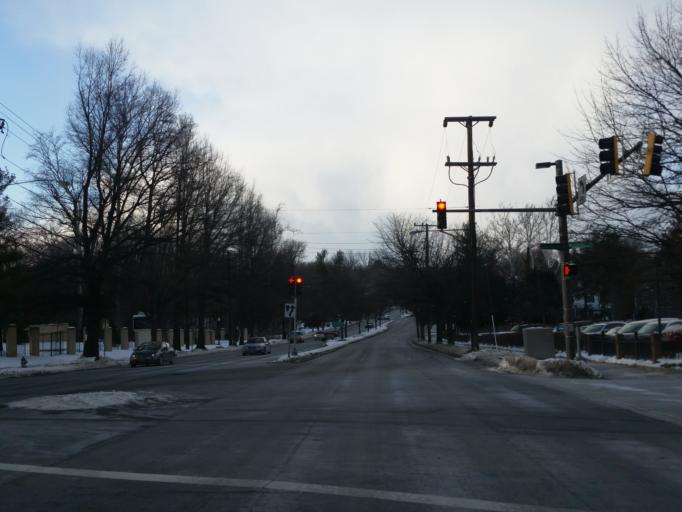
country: US
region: Maryland
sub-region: Montgomery County
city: Friendship Village
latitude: 38.9653
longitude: -77.0879
